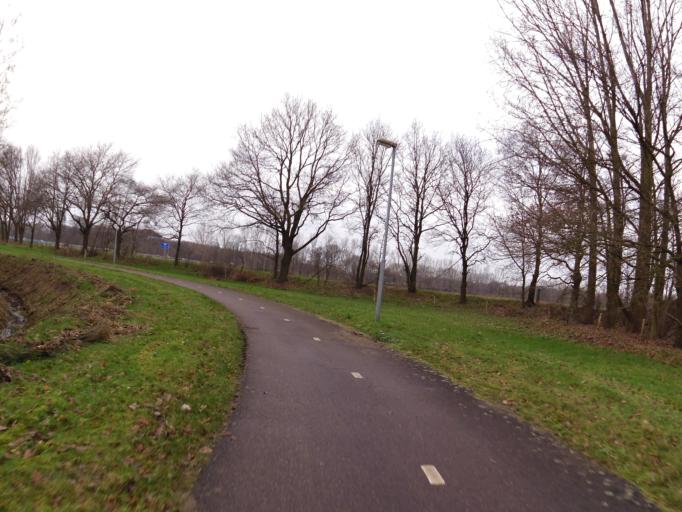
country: NL
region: North Brabant
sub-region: Gemeente Vught
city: Vught
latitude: 51.6327
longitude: 5.3142
